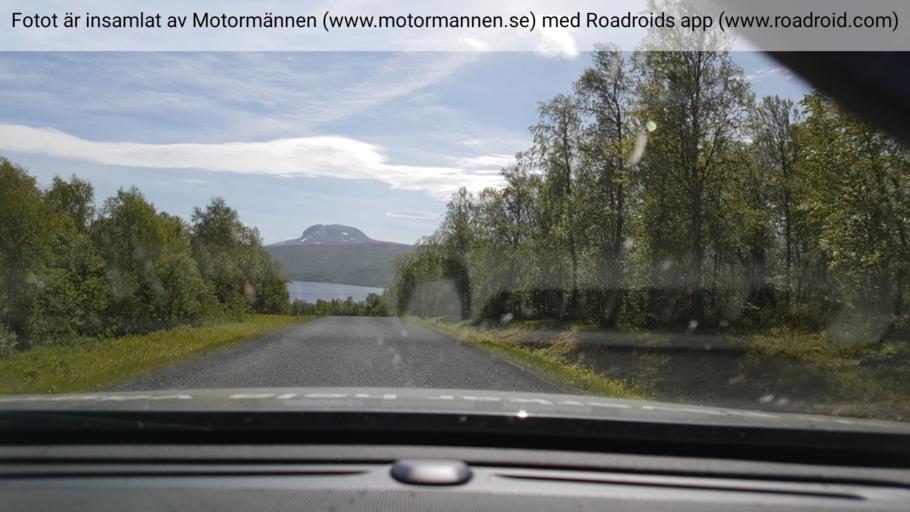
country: NO
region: Nordland
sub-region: Hattfjelldal
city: Hattfjelldal
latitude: 65.3413
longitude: 15.0996
